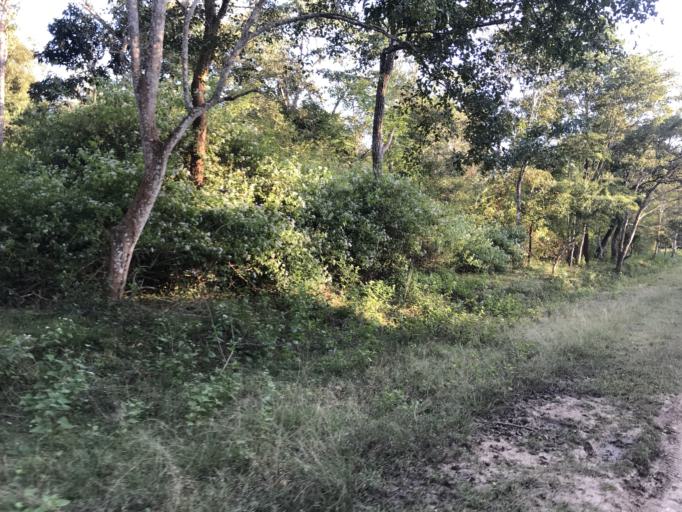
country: IN
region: Karnataka
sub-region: Mysore
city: Heggadadevankote
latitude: 11.9975
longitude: 76.2454
